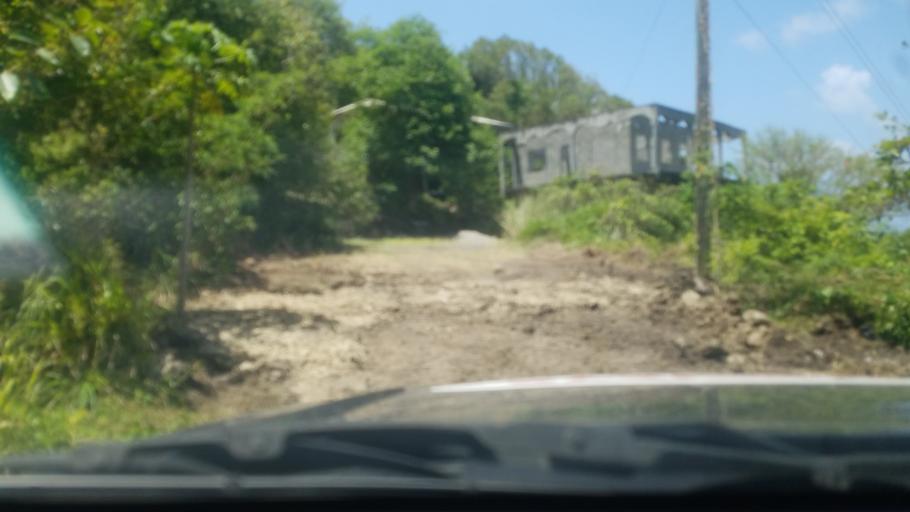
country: LC
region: Vieux-Fort
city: Vieux Fort
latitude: 13.7394
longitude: -60.9434
